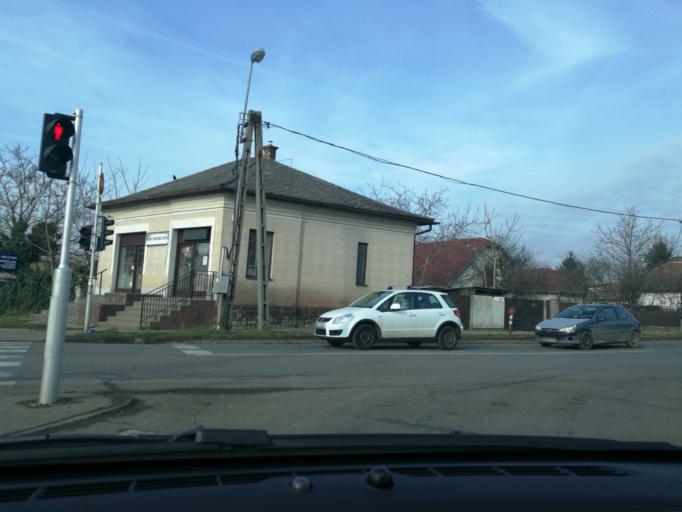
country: HU
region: Szabolcs-Szatmar-Bereg
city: Nyiregyhaza
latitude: 47.9523
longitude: 21.7345
